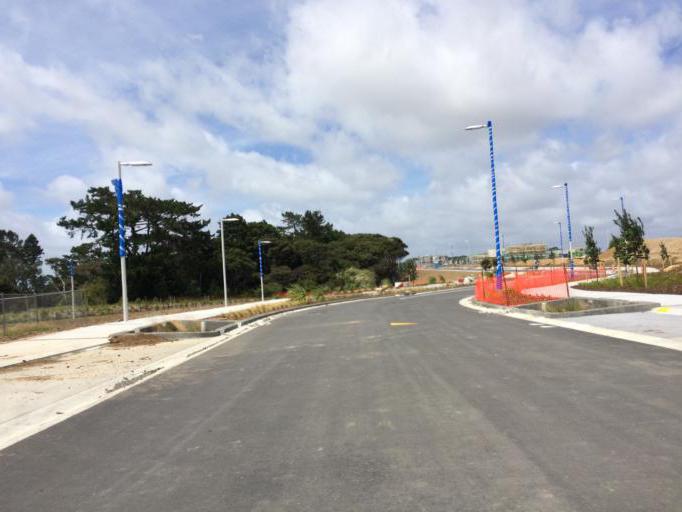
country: NZ
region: Auckland
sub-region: Auckland
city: North Shore
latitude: -36.7912
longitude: 174.6699
